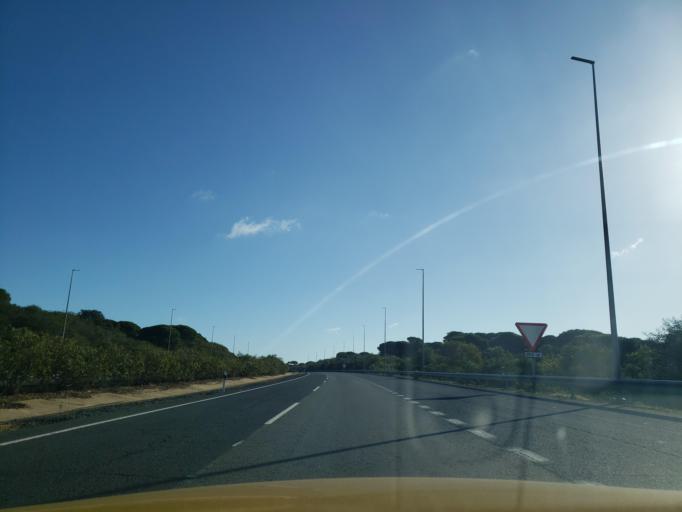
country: ES
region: Andalusia
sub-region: Provincia de Huelva
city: Cartaya
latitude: 37.3225
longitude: -7.1123
